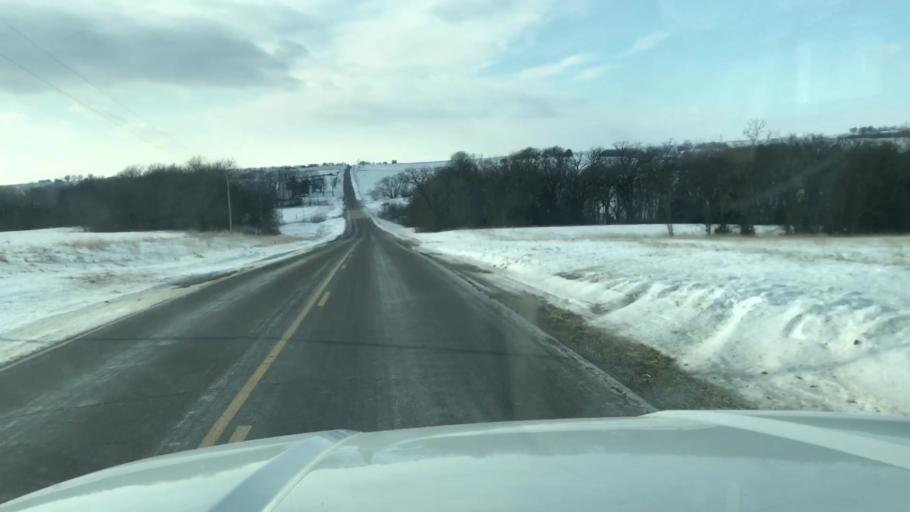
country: US
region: Missouri
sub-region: Nodaway County
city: Maryville
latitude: 40.2008
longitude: -94.8900
